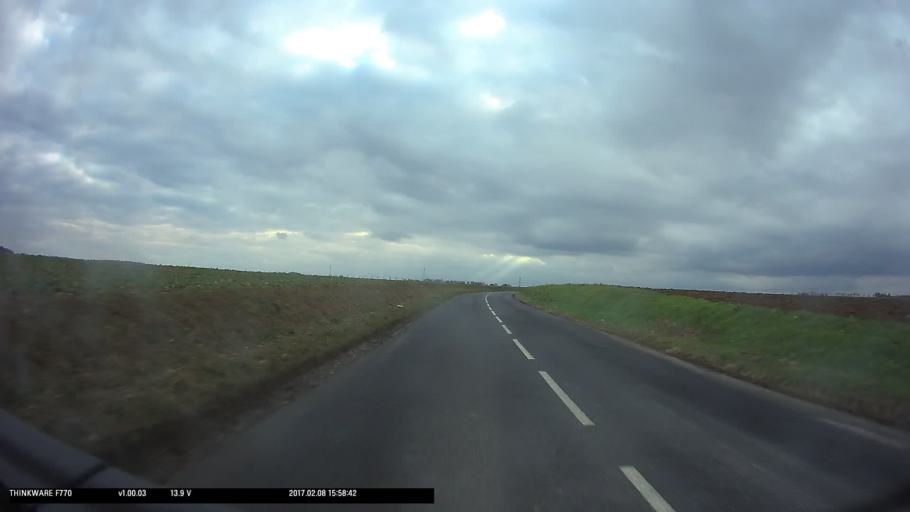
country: FR
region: Ile-de-France
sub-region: Departement du Val-d'Oise
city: Vigny
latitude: 49.0902
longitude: 1.9407
